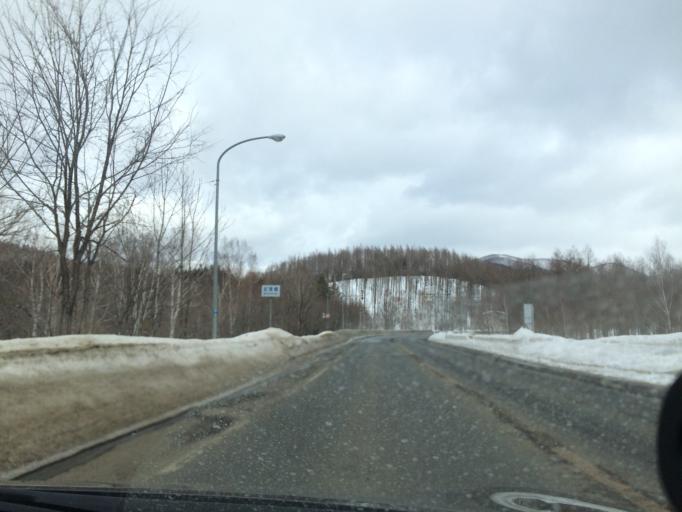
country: JP
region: Hokkaido
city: Shimo-furano
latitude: 43.1290
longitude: 142.6795
